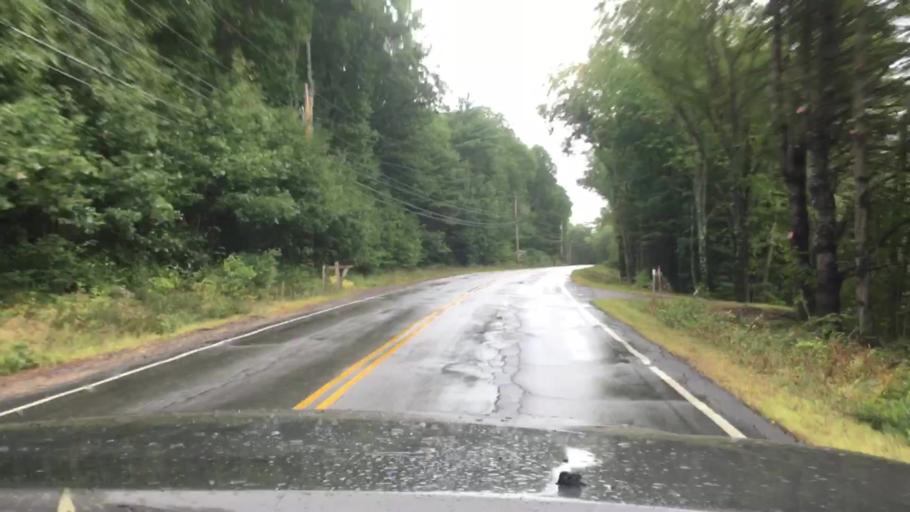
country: US
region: New Hampshire
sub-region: Belknap County
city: Meredith
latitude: 43.6496
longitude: -71.5426
